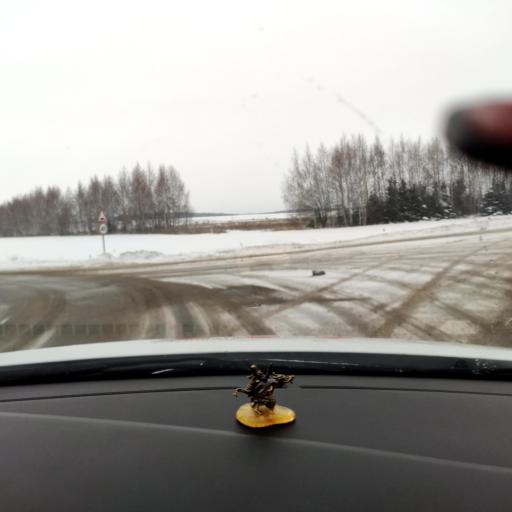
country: RU
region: Tatarstan
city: Vysokaya Gora
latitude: 56.1075
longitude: 49.1780
